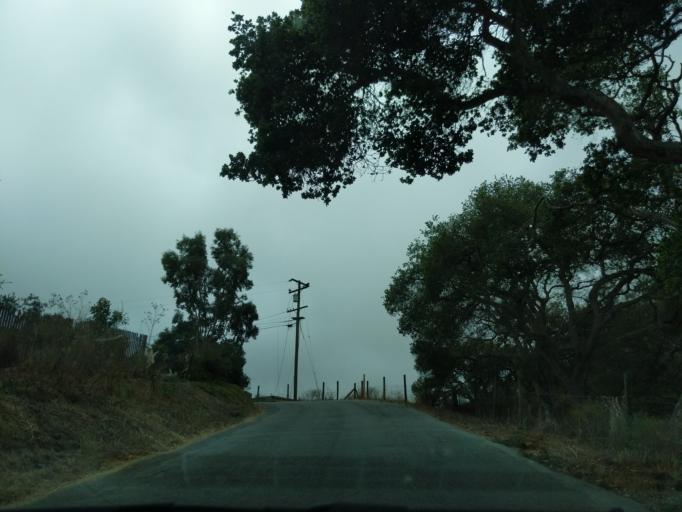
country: US
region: California
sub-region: Monterey County
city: Prunedale
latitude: 36.7924
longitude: -121.7012
